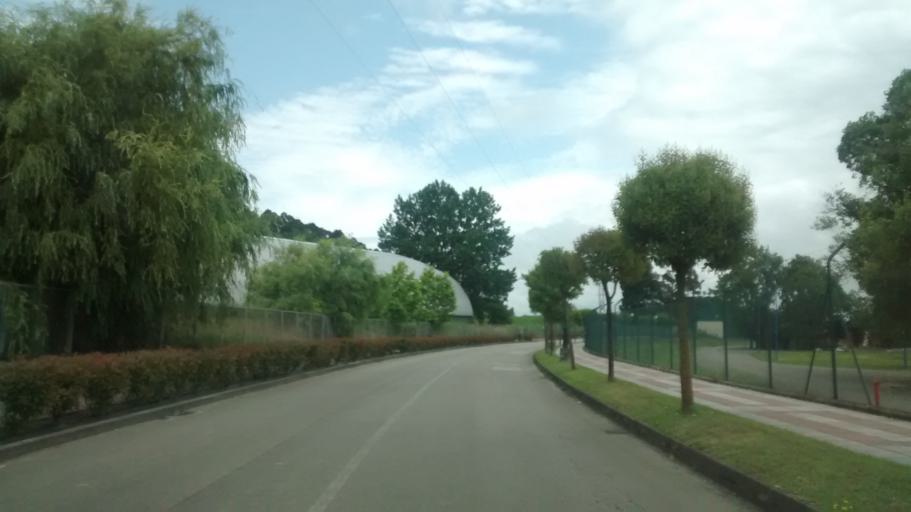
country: ES
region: Cantabria
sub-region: Provincia de Cantabria
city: El Astillero
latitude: 43.4170
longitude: -3.8197
